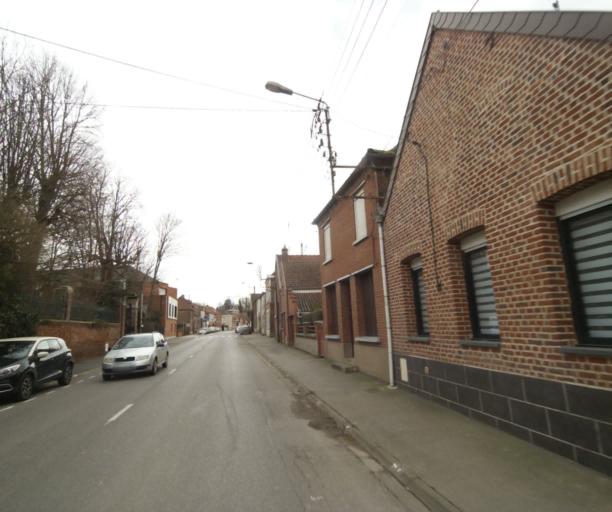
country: FR
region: Nord-Pas-de-Calais
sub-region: Departement du Nord
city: Curgies
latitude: 50.3301
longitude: 3.6024
